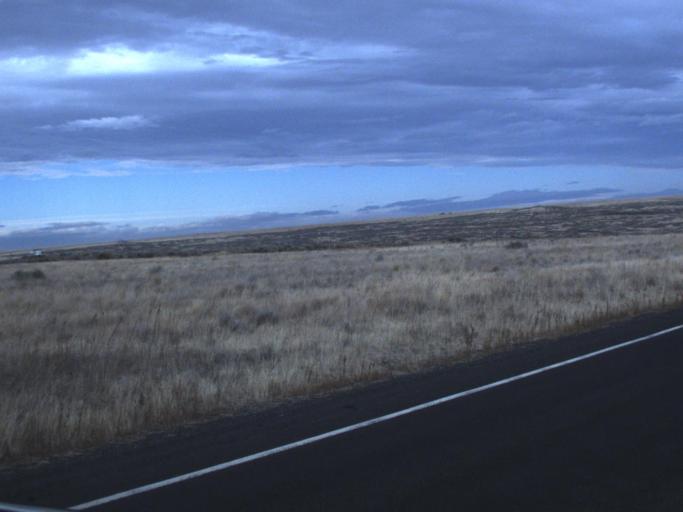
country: US
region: Washington
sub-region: Adams County
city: Ritzville
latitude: 47.4046
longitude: -118.6848
